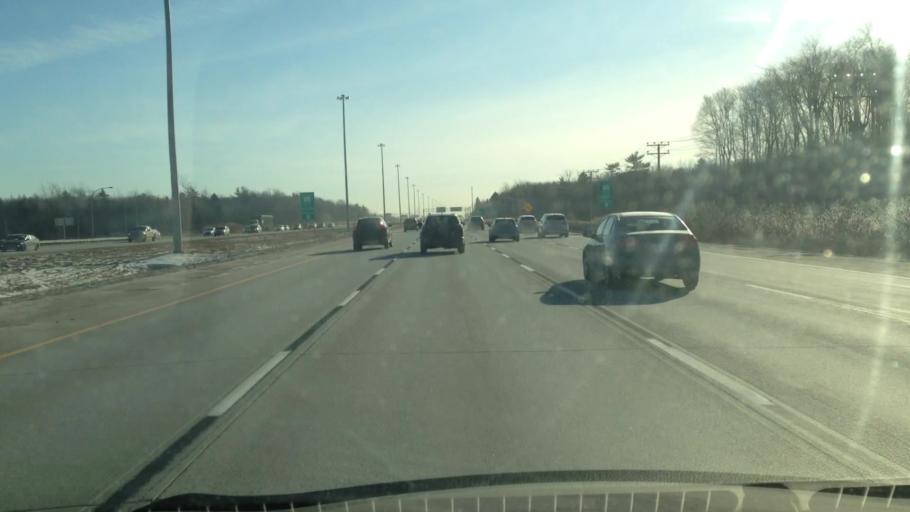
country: CA
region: Quebec
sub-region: Laurentides
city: Blainville
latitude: 45.6606
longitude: -73.8899
